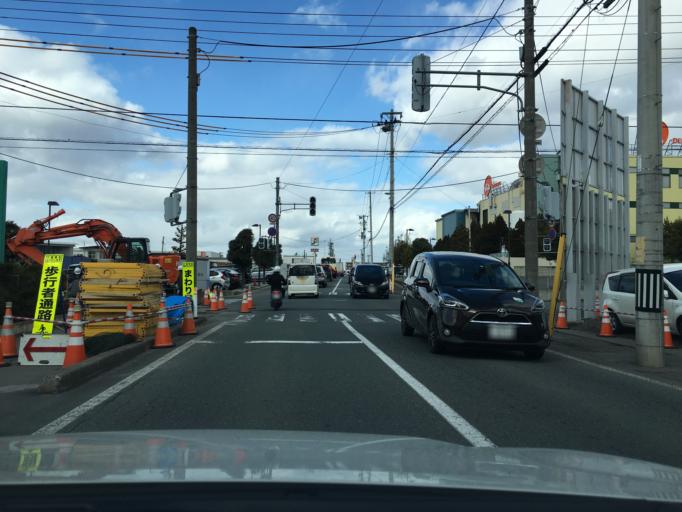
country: JP
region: Yamagata
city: Yamagata-shi
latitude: 38.2517
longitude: 140.3143
